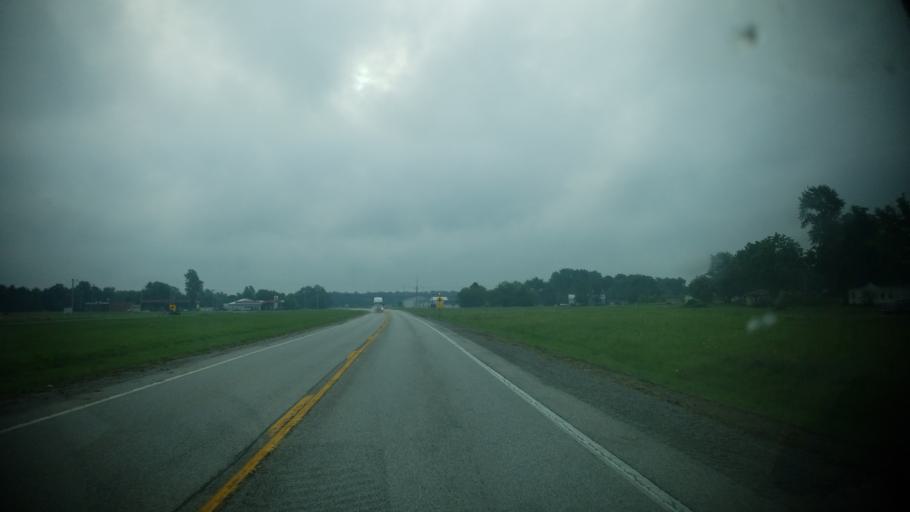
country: US
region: Illinois
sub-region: Clay County
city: Flora
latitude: 38.6787
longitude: -88.3584
